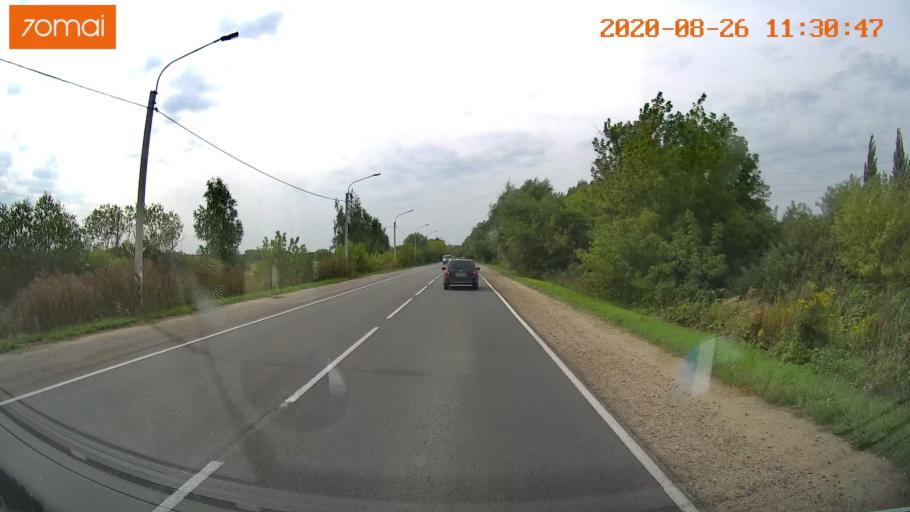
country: RU
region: Rjazan
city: Shilovo
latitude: 54.3127
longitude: 40.8790
